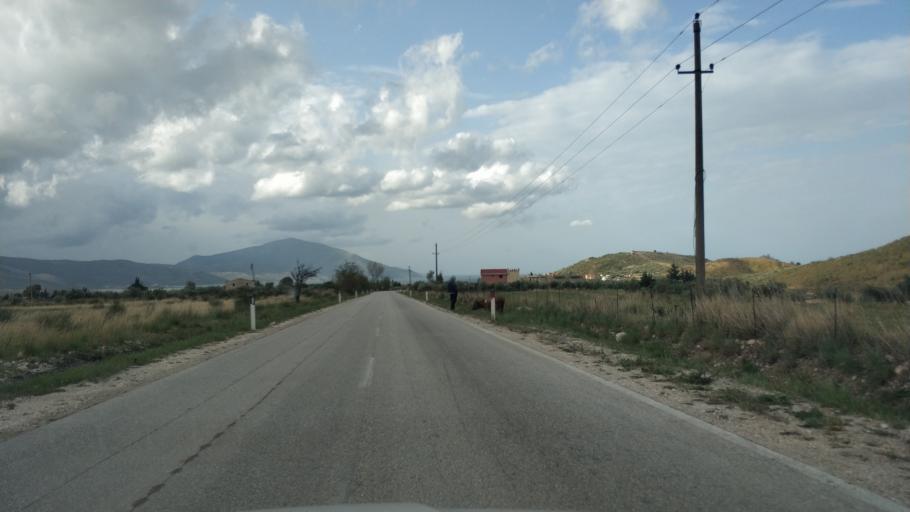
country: AL
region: Vlore
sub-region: Rrethi i Vlores
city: Orikum
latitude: 40.2870
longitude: 19.4953
